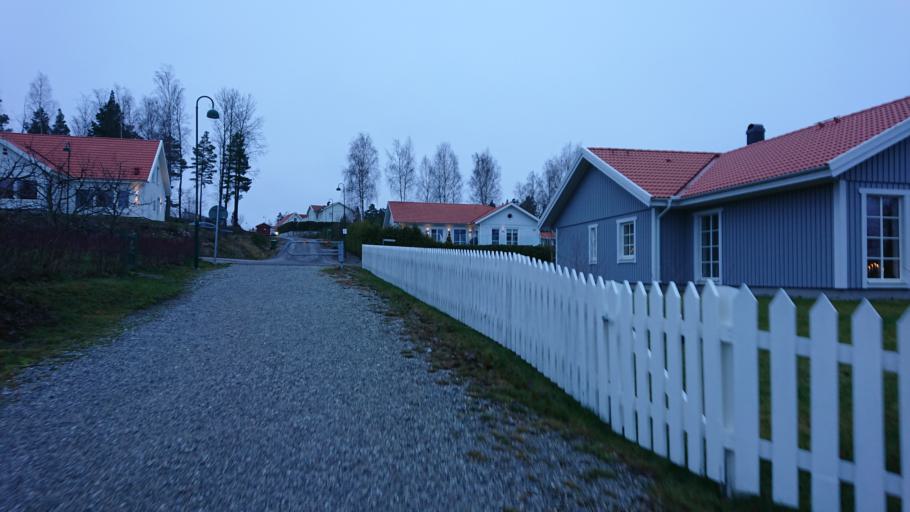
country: SE
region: Soedermanland
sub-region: Strangnas Kommun
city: Stallarholmen
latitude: 59.3658
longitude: 17.1870
